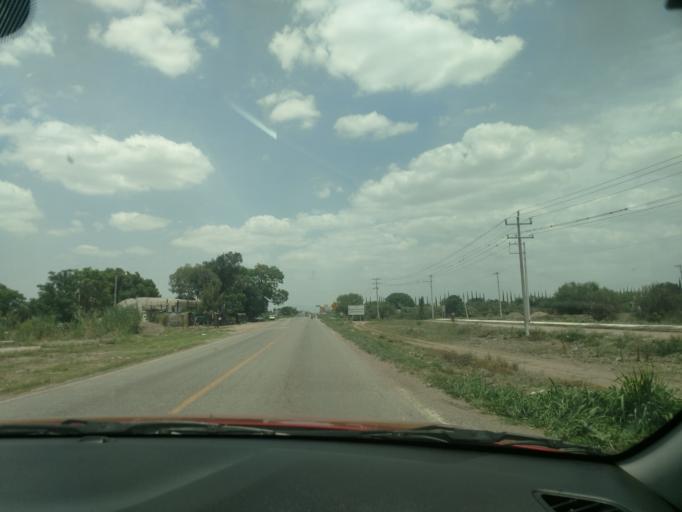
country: MX
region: San Luis Potosi
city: Ciudad Fernandez
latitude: 21.9432
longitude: -100.0454
